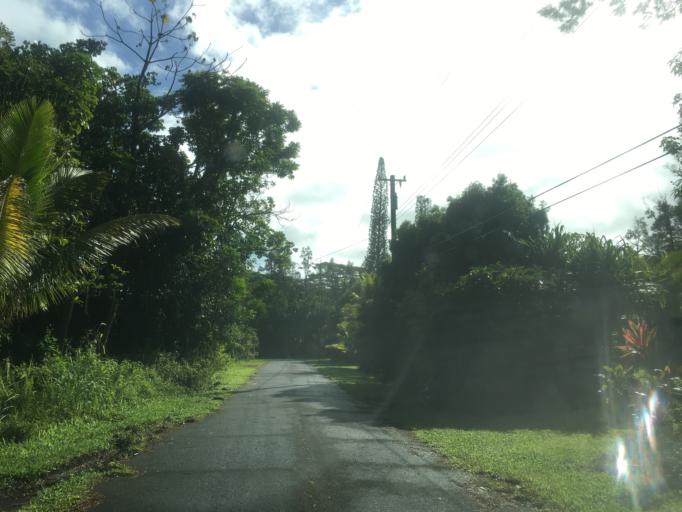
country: US
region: Hawaii
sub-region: Hawaii County
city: Leilani Estates
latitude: 19.4860
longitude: -154.9246
